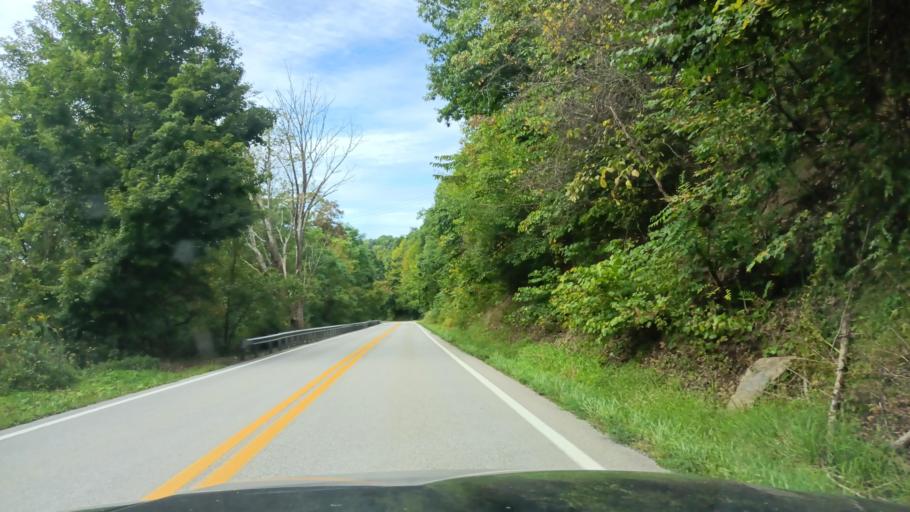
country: US
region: West Virginia
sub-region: Harrison County
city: Bridgeport
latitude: 39.3036
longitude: -80.1644
